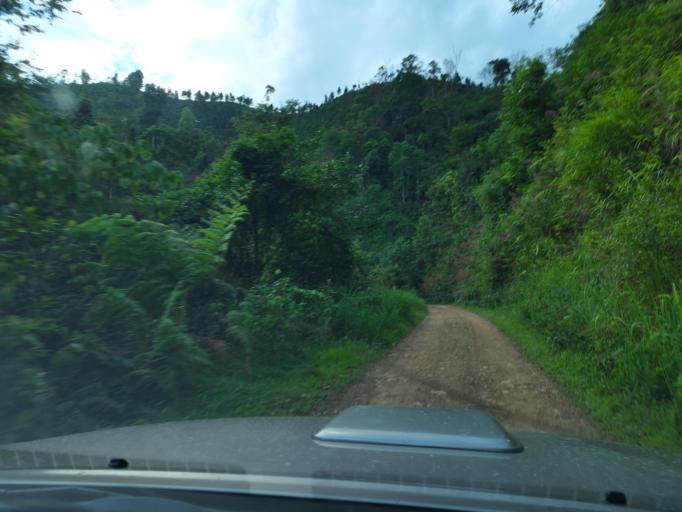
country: LA
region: Phongsali
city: Phongsali
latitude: 21.6532
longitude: 102.1475
